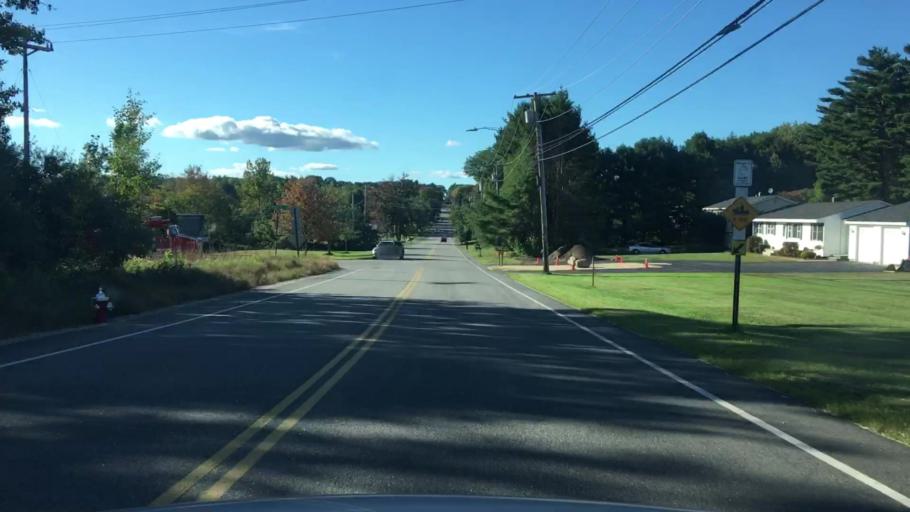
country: US
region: Maine
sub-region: Androscoggin County
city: Lewiston
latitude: 44.0784
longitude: -70.1630
